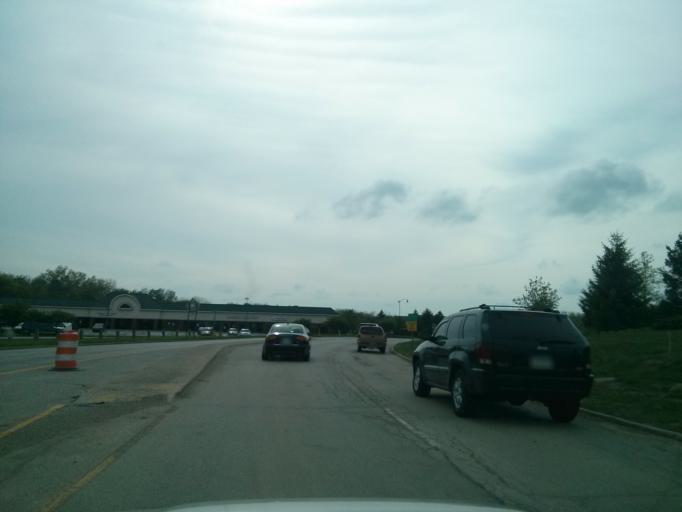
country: US
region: Indiana
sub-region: Hamilton County
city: Carmel
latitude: 39.9714
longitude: -86.1583
